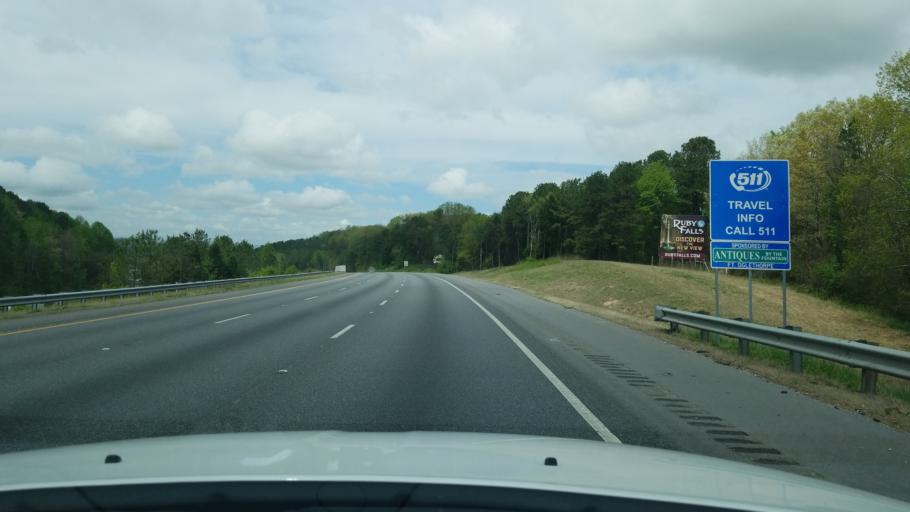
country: US
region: Georgia
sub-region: Catoosa County
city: Indian Springs
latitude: 34.9345
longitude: -85.1556
